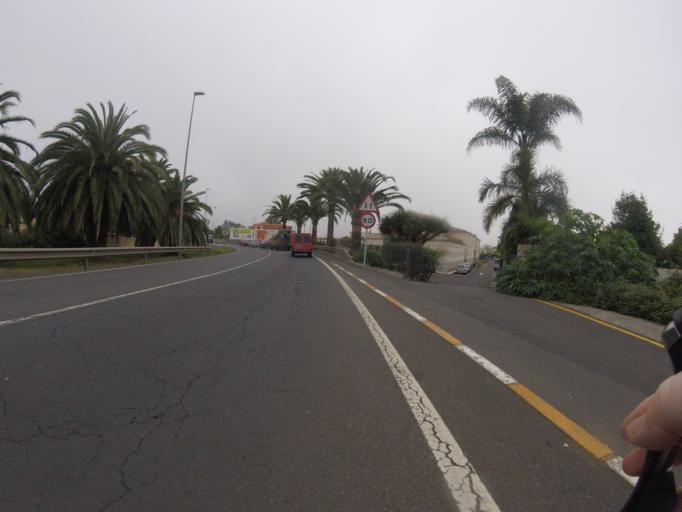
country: ES
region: Canary Islands
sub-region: Provincia de Santa Cruz de Tenerife
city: Tacoronte
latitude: 28.4923
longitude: -16.3702
